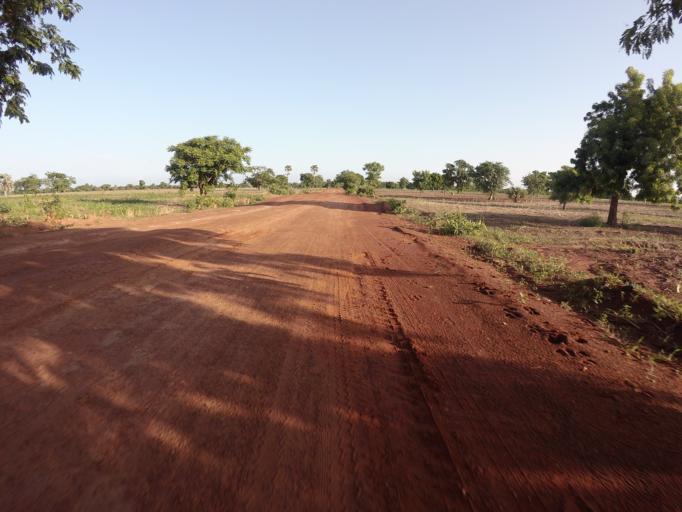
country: TG
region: Savanes
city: Sansanne-Mango
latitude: 10.3465
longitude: -0.0927
